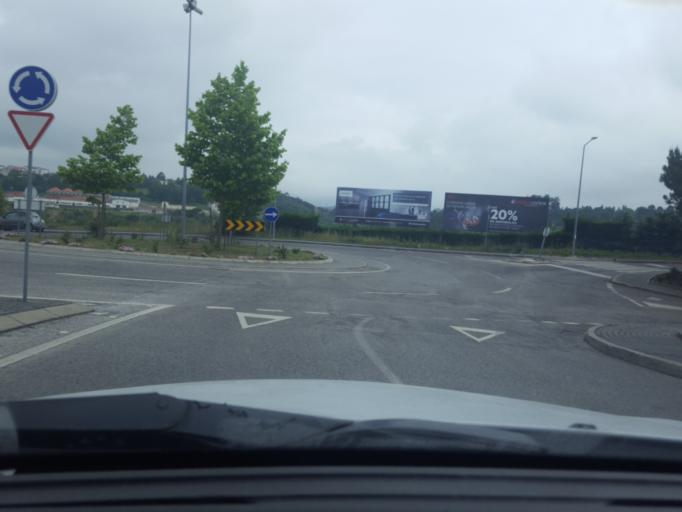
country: PT
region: Leiria
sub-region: Leiria
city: Leiria
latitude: 39.7328
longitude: -8.8226
